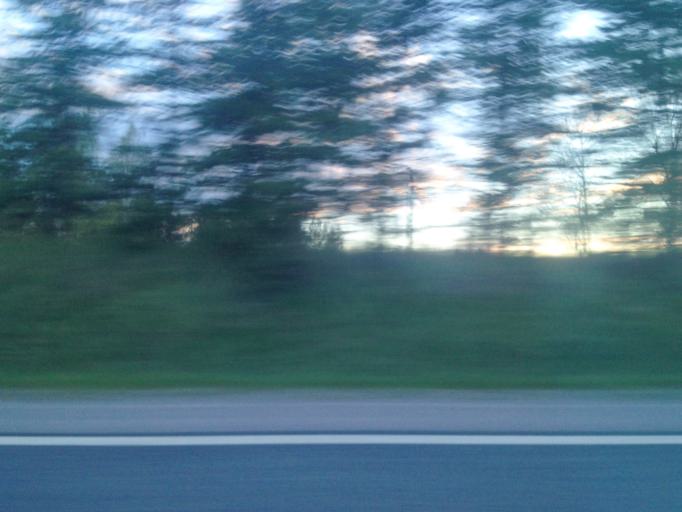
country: FI
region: Uusimaa
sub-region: Helsinki
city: Nurmijaervi
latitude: 60.3492
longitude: 24.8098
